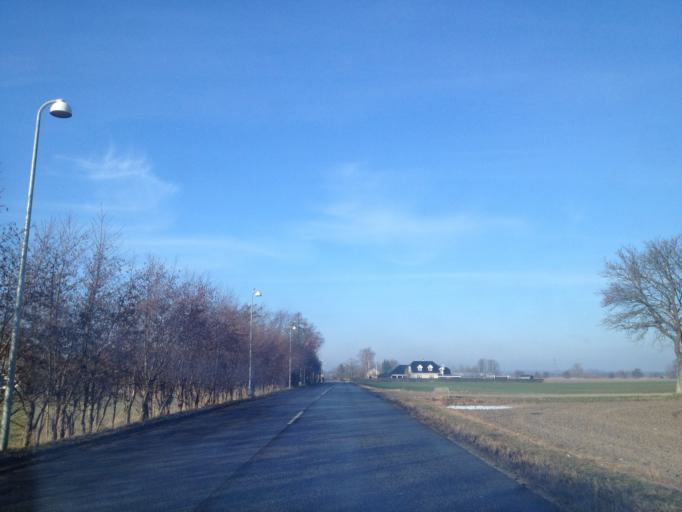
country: DK
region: Zealand
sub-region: Greve Kommune
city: Greve
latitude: 55.6069
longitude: 12.2873
